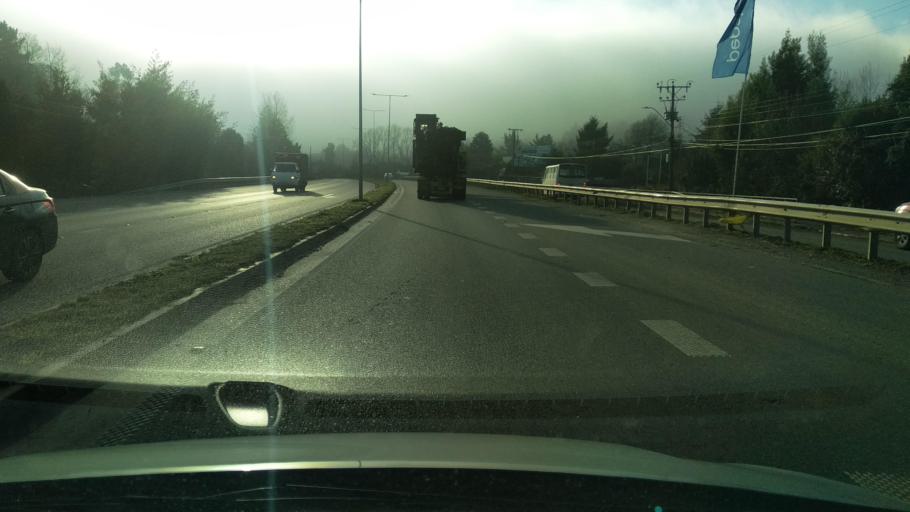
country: CL
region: Los Lagos
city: Las Animas
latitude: -39.7724
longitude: -73.2200
